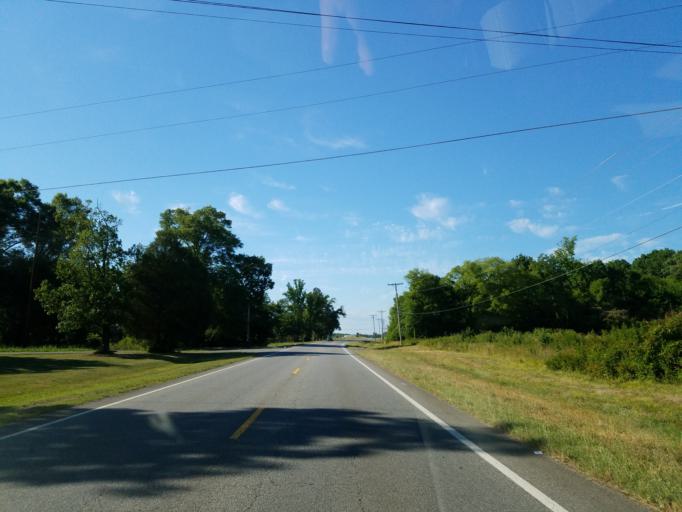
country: US
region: Georgia
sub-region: Gordon County
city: Calhoun
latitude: 34.4403
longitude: -84.9357
